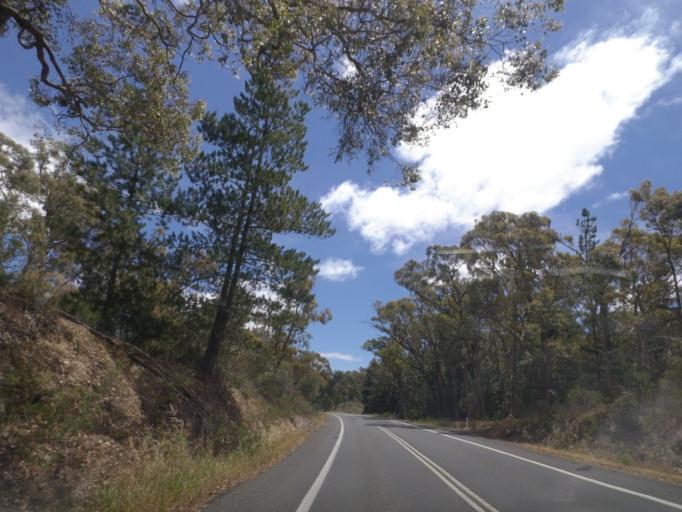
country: AU
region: Victoria
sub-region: Mount Alexander
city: Castlemaine
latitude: -37.2837
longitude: 144.1596
